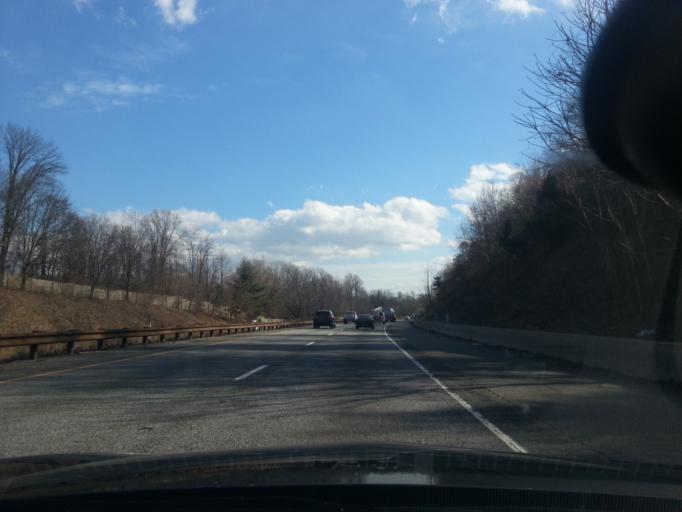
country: US
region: Pennsylvania
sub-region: Delaware County
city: Broomall
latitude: 39.9684
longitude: -75.3360
